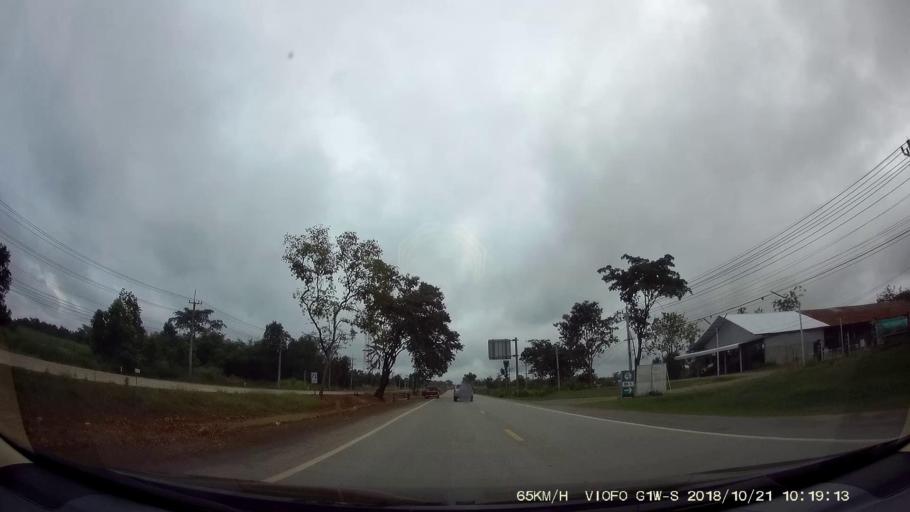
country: TH
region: Chaiyaphum
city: Phu Khiao
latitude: 16.3165
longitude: 102.1970
